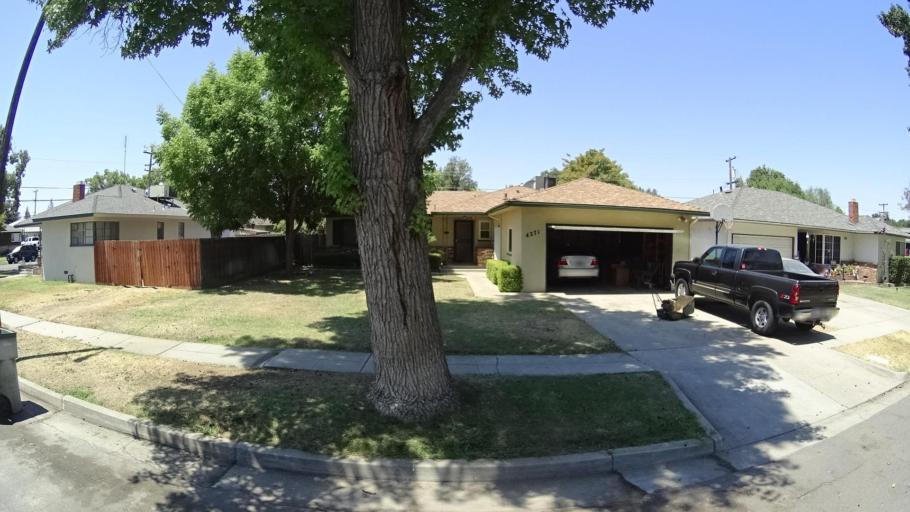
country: US
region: California
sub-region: Fresno County
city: Fresno
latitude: 36.7954
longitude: -119.7660
